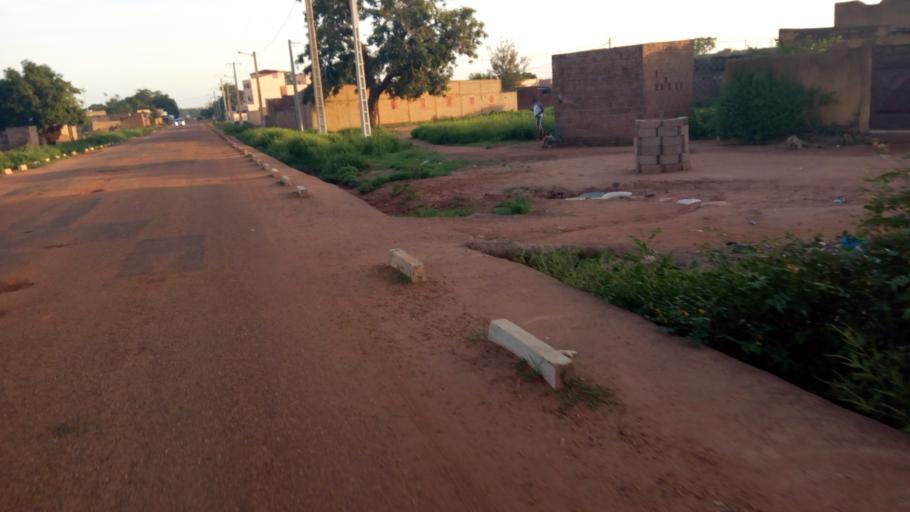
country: ML
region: Sikasso
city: Koutiala
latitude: 12.4090
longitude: -5.4451
